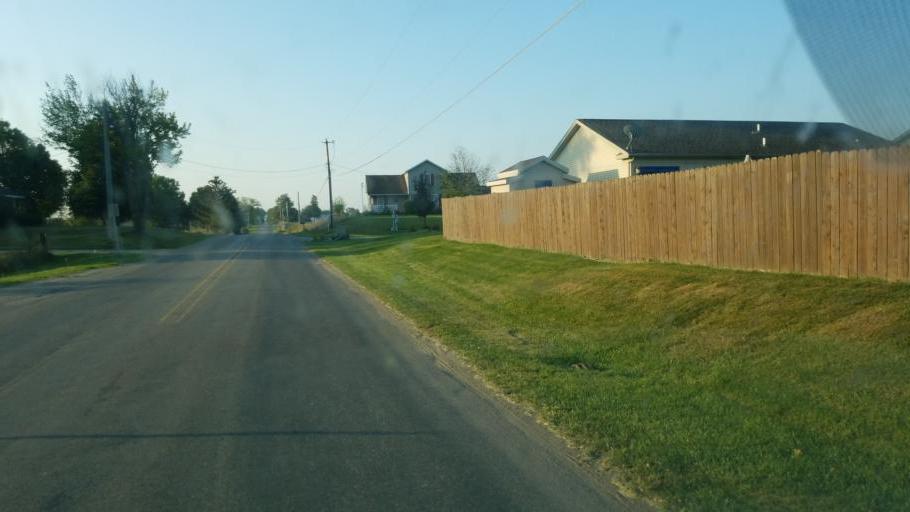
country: US
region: Indiana
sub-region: LaGrange County
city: Lagrange
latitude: 41.6331
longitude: -85.4248
